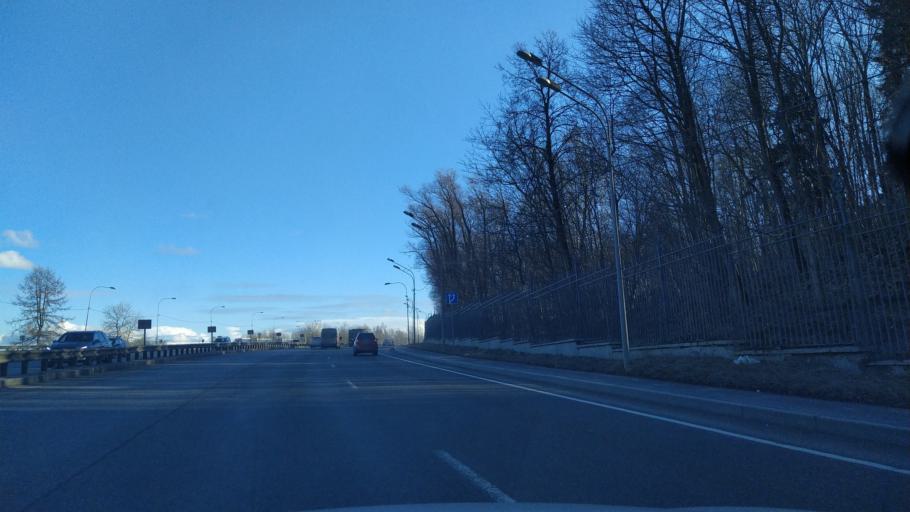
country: RU
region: St.-Petersburg
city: Aleksandrovskaya
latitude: 59.7734
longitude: 30.3305
